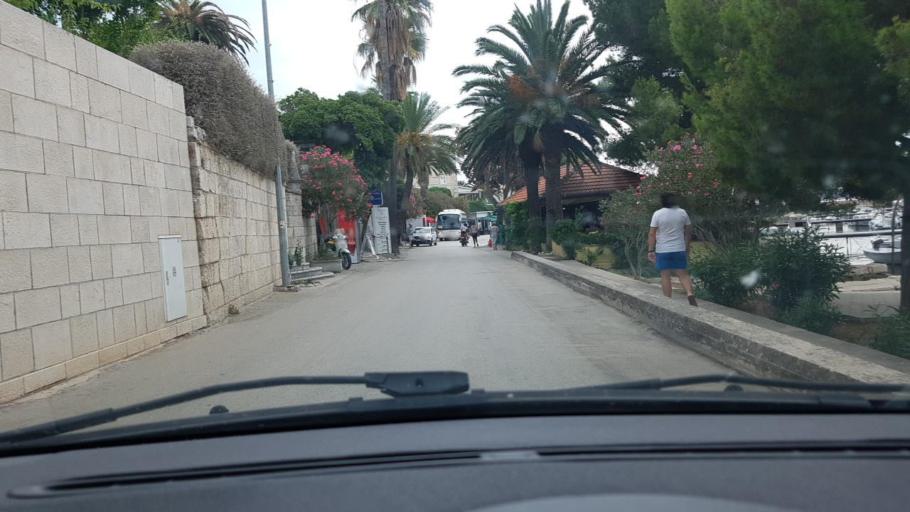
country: HR
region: Dubrovacko-Neretvanska
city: Orebic
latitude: 42.9748
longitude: 17.1751
